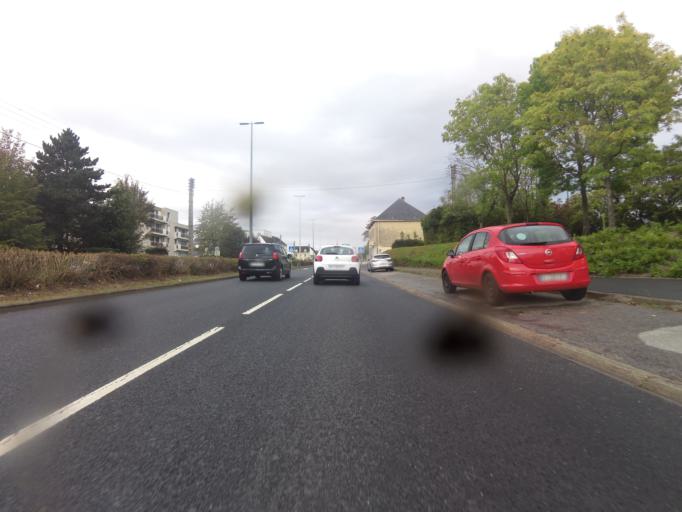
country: FR
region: Lower Normandy
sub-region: Departement du Calvados
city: Saint-Germain-la-Blanche-Herbe
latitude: 49.1817
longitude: -0.3875
